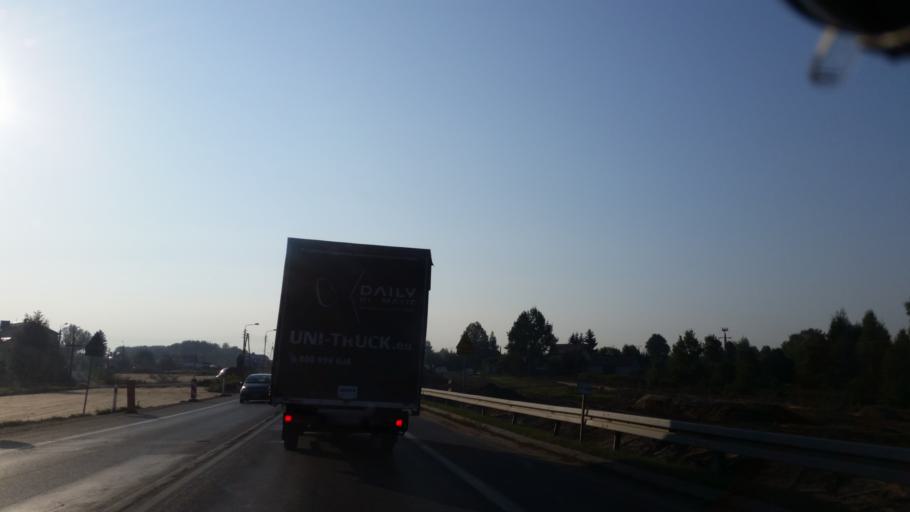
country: PL
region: Masovian Voivodeship
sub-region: Powiat otwocki
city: Otwock
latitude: 52.1388
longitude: 21.3325
